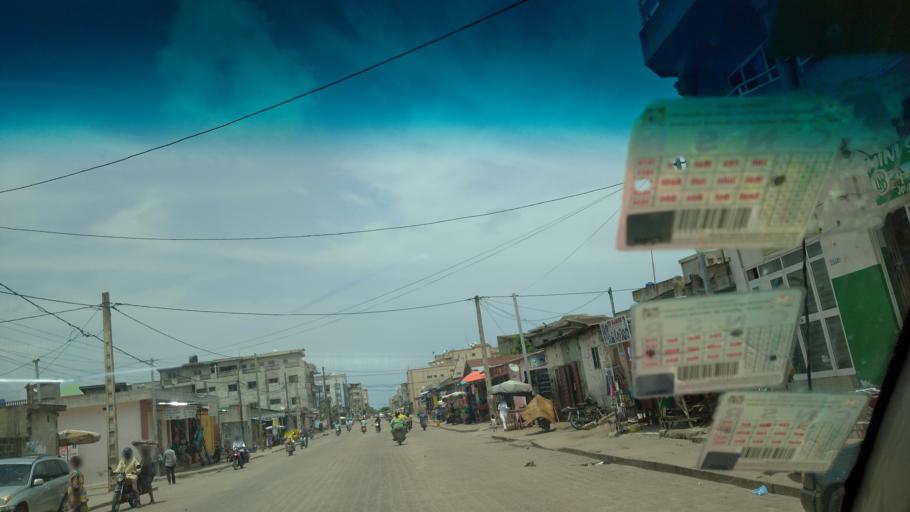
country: BJ
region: Littoral
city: Cotonou
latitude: 6.3924
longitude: 2.4521
